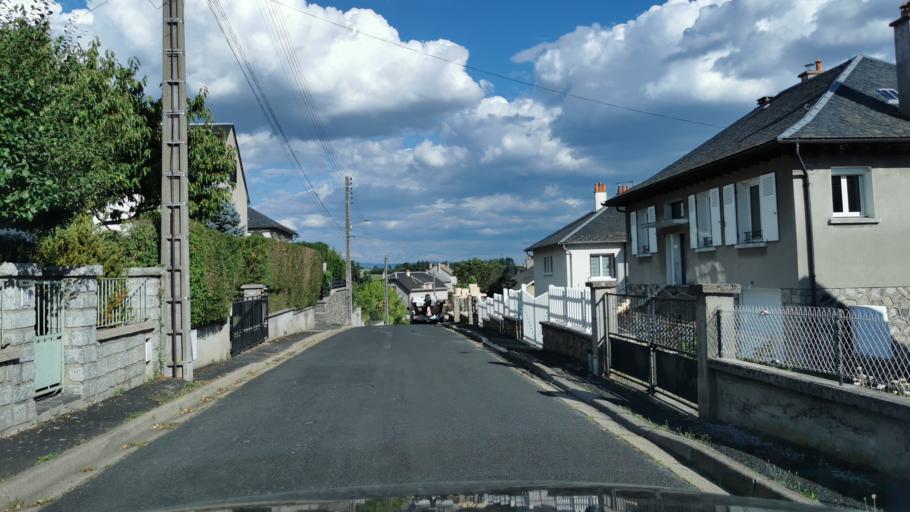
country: FR
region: Auvergne
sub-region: Departement du Cantal
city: Saint-Flour
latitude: 45.0380
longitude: 3.1055
